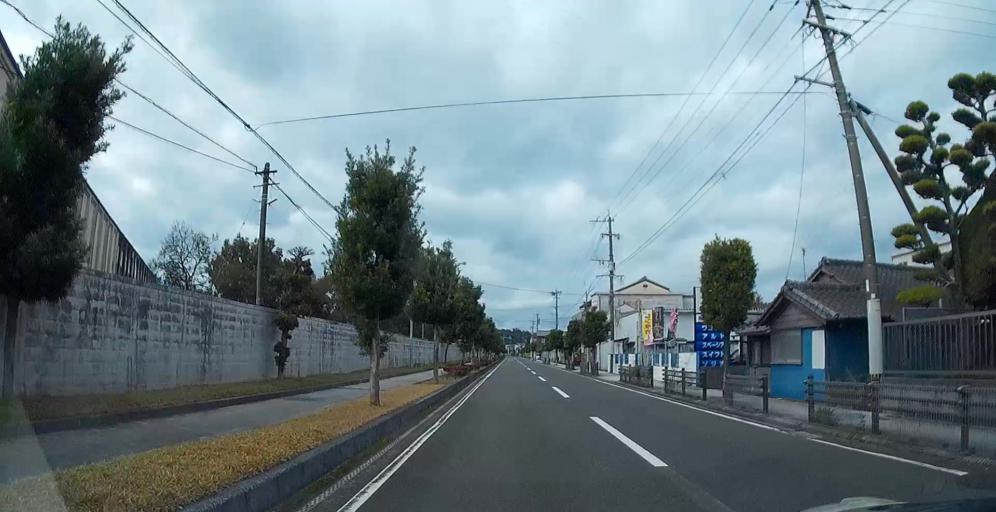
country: JP
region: Kumamoto
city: Minamata
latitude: 32.2111
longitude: 130.3936
